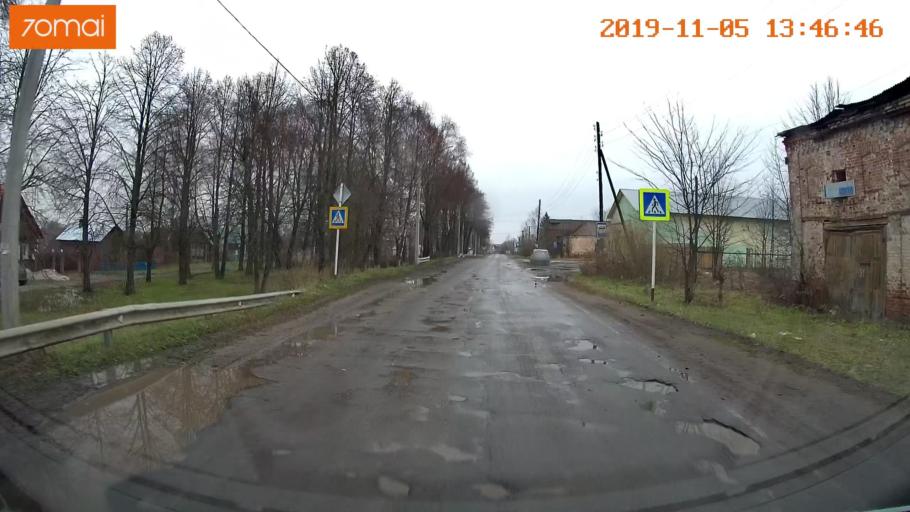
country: RU
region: Ivanovo
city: Shuya
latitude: 56.9971
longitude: 41.4100
